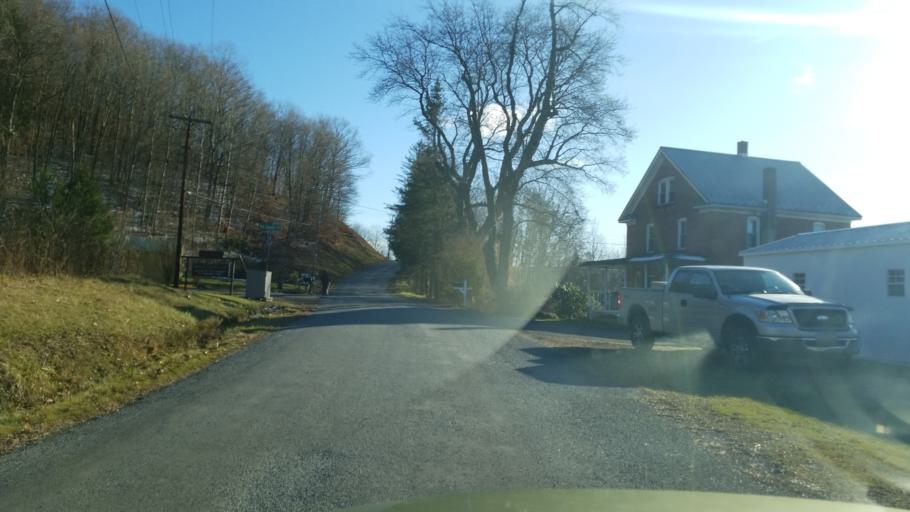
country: US
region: Pennsylvania
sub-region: Jefferson County
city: Brockway
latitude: 41.2582
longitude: -78.7984
